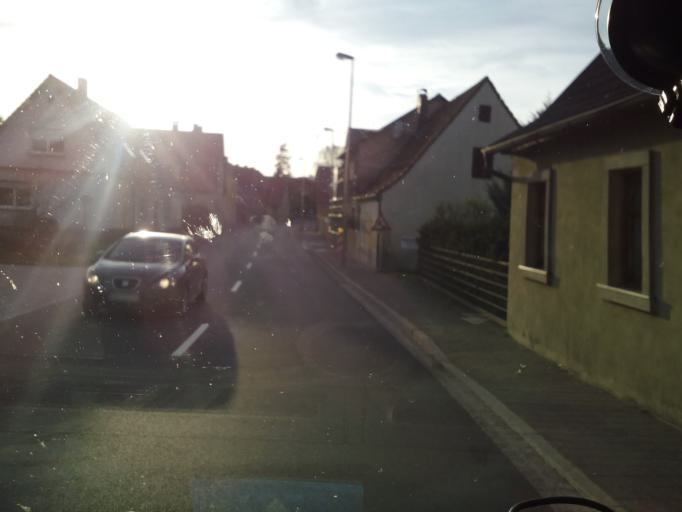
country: DE
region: Bavaria
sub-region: Upper Franconia
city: Baunach
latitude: 49.9886
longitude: 10.8494
